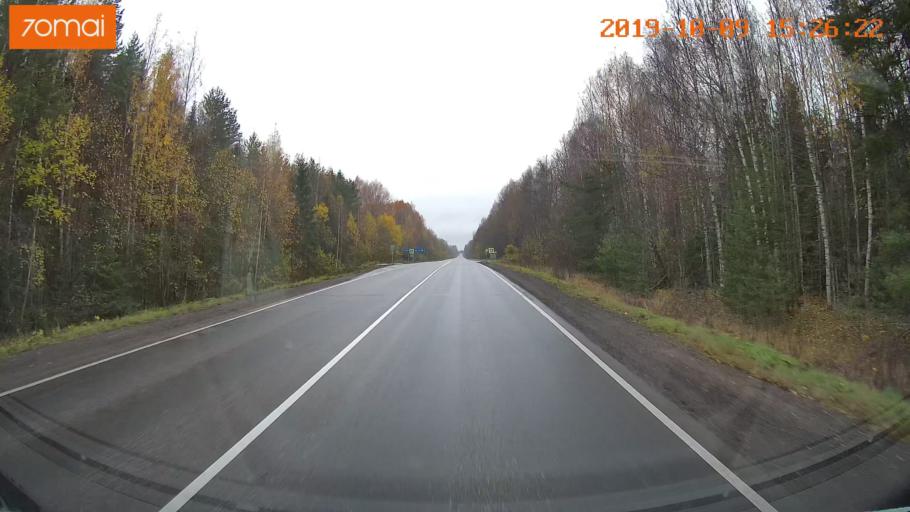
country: RU
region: Kostroma
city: Susanino
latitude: 58.0206
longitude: 41.4057
